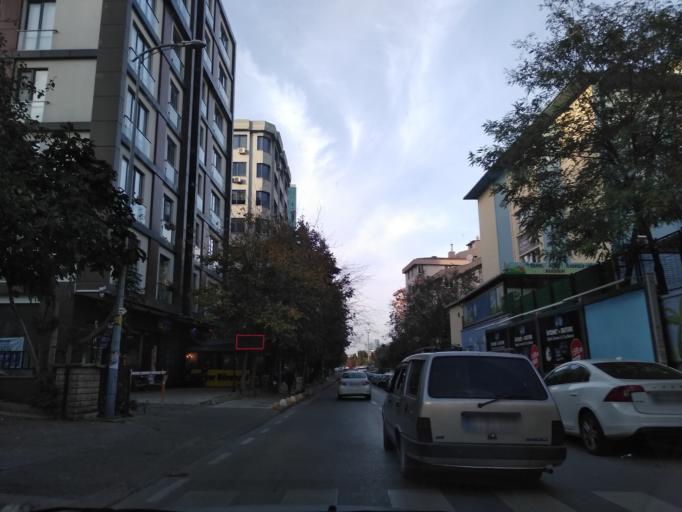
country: TR
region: Istanbul
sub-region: Atasehir
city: Atasehir
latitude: 40.9790
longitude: 29.0923
